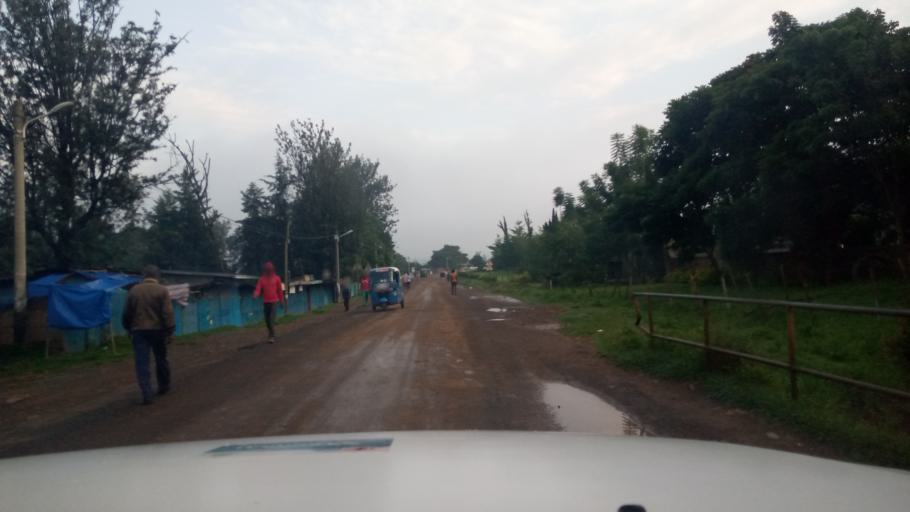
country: ET
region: Oromiya
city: Jima
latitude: 7.6769
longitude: 36.8519
